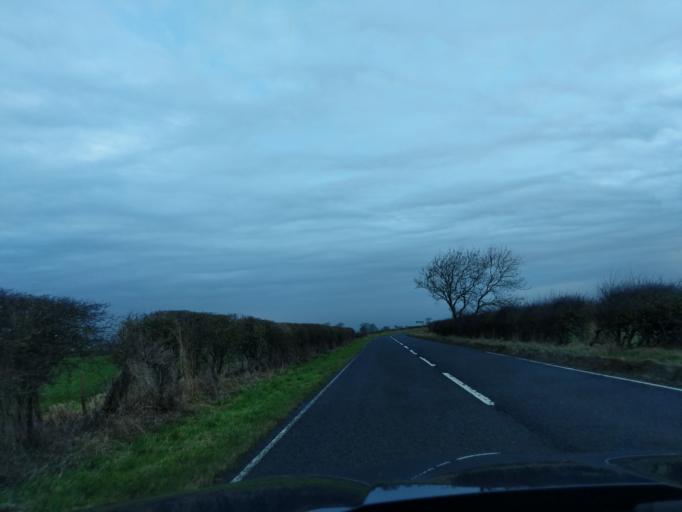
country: GB
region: England
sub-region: Northumberland
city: Rothley
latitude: 55.1311
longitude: -1.9545
